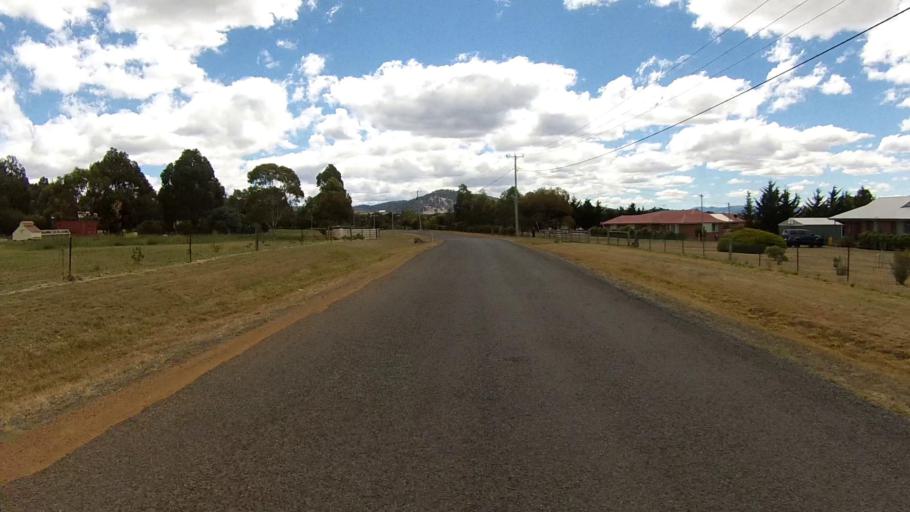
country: AU
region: Tasmania
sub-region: Clarence
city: Seven Mile Beach
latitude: -42.8502
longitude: 147.4757
